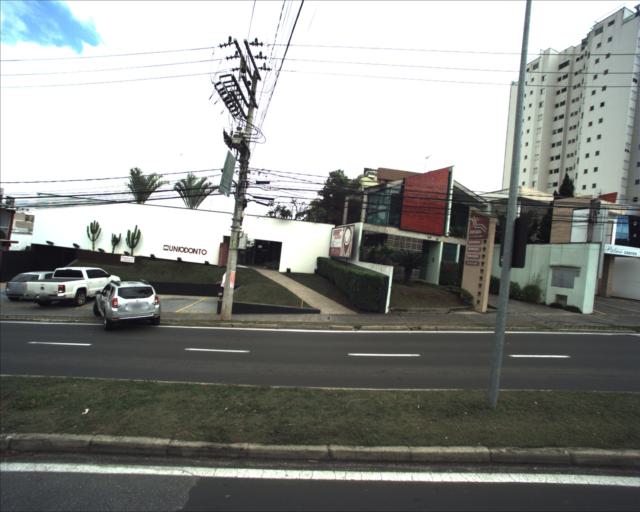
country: BR
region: Sao Paulo
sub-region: Sorocaba
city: Sorocaba
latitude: -23.5089
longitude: -47.4620
